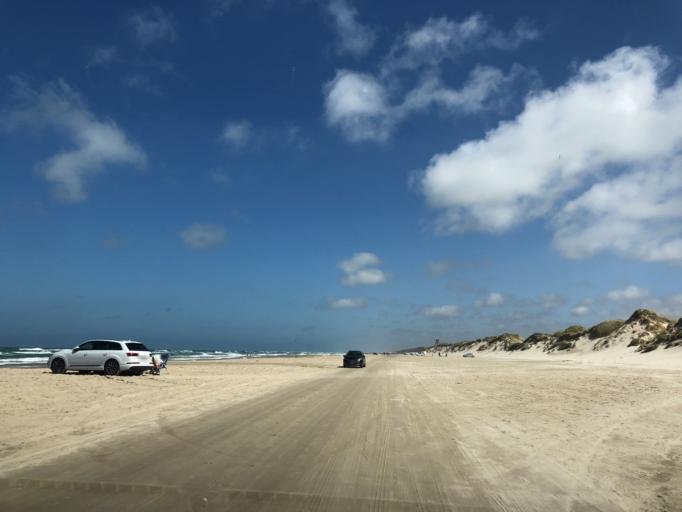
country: DK
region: North Denmark
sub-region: Jammerbugt Kommune
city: Pandrup
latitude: 57.2478
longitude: 9.5705
